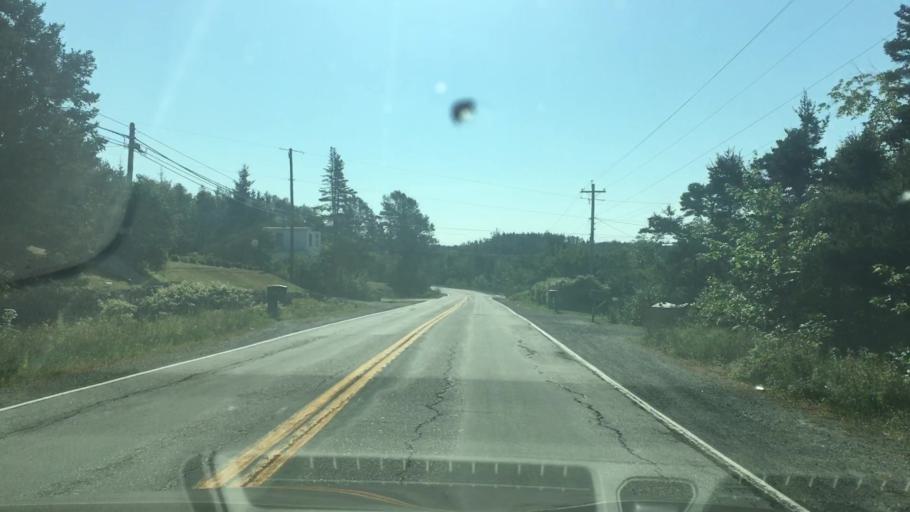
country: CA
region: Nova Scotia
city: Cole Harbour
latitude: 44.7766
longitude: -63.0567
